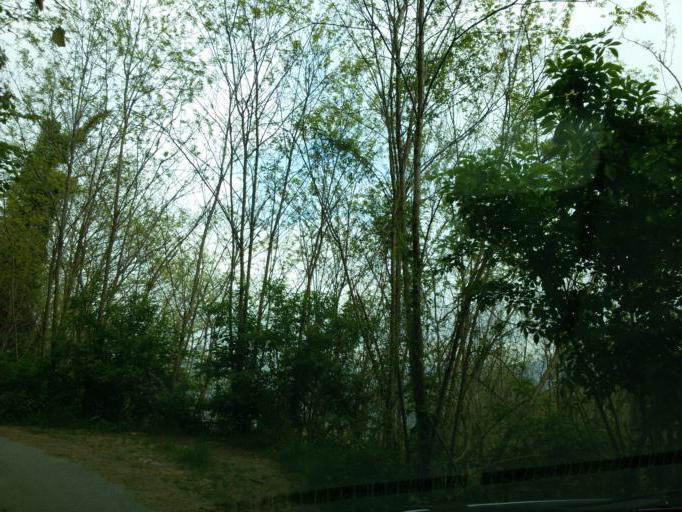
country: IT
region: Liguria
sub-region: Provincia di Genova
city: Santa Marta
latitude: 44.4762
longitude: 8.8811
